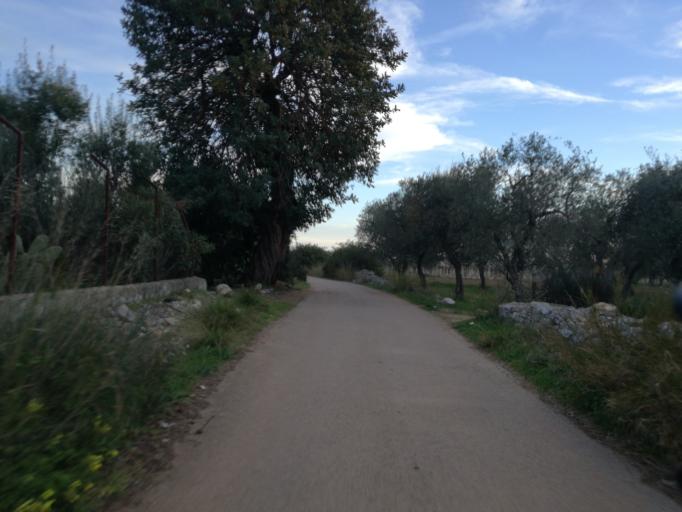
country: IT
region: Apulia
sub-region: Provincia di Bari
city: Lamie
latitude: 41.0228
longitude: 16.8718
